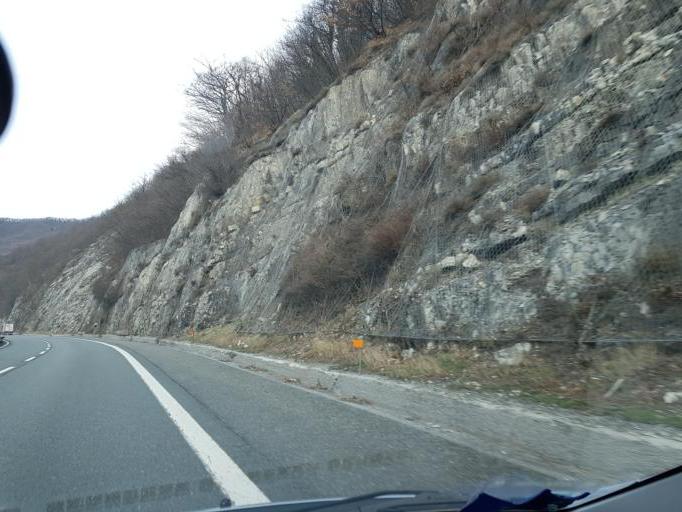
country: IT
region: Liguria
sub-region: Provincia di Genova
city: Ronco Scrivia
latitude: 44.6246
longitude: 8.9505
